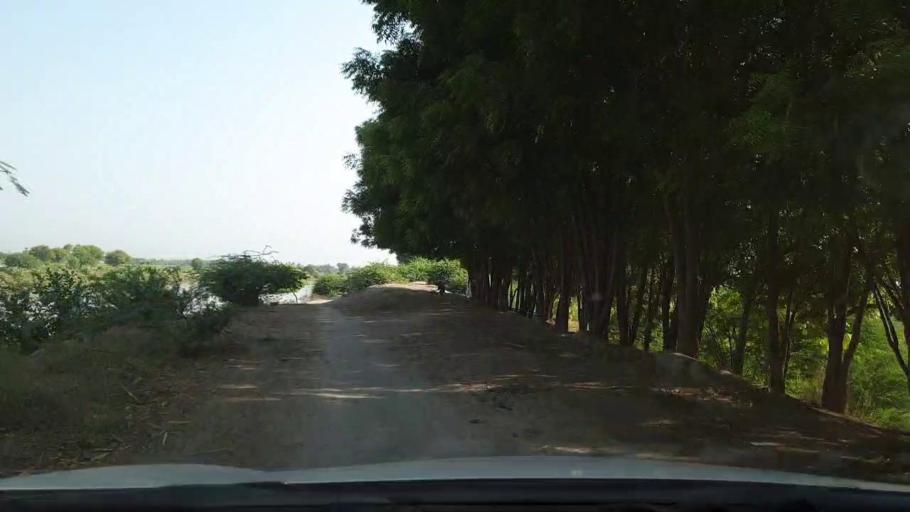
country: PK
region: Sindh
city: Larkana
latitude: 27.5599
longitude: 68.2578
